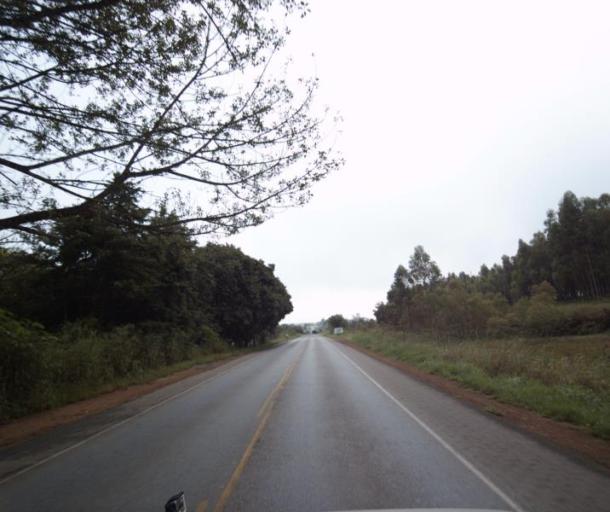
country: BR
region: Goias
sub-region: Pirenopolis
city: Pirenopolis
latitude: -15.8015
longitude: -48.7788
